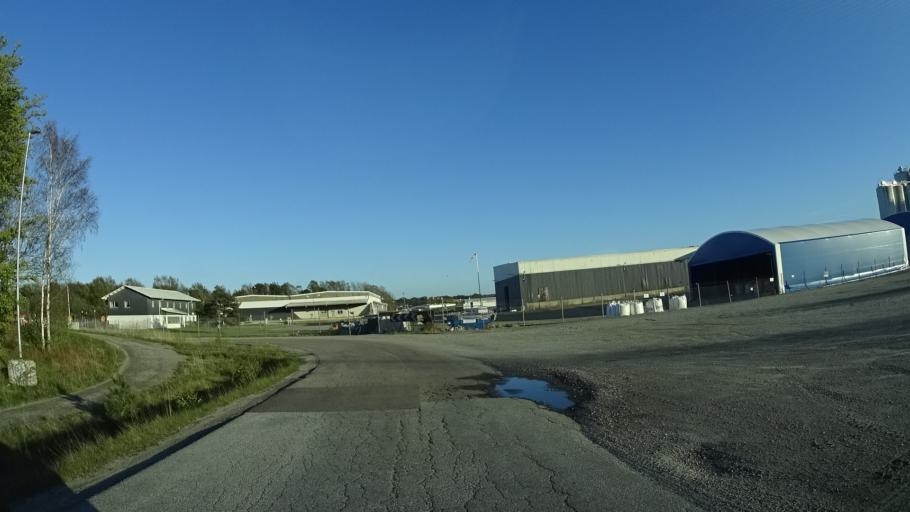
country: SE
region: Vaestra Goetaland
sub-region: Stenungsunds Kommun
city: Stenungsund
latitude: 58.0826
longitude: 11.8163
